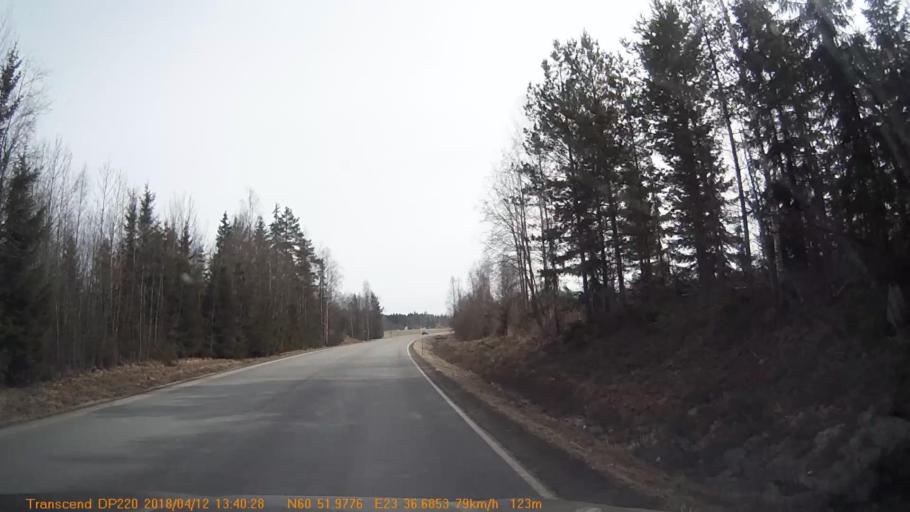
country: FI
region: Haeme
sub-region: Forssa
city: Forssa
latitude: 60.8656
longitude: 23.6122
